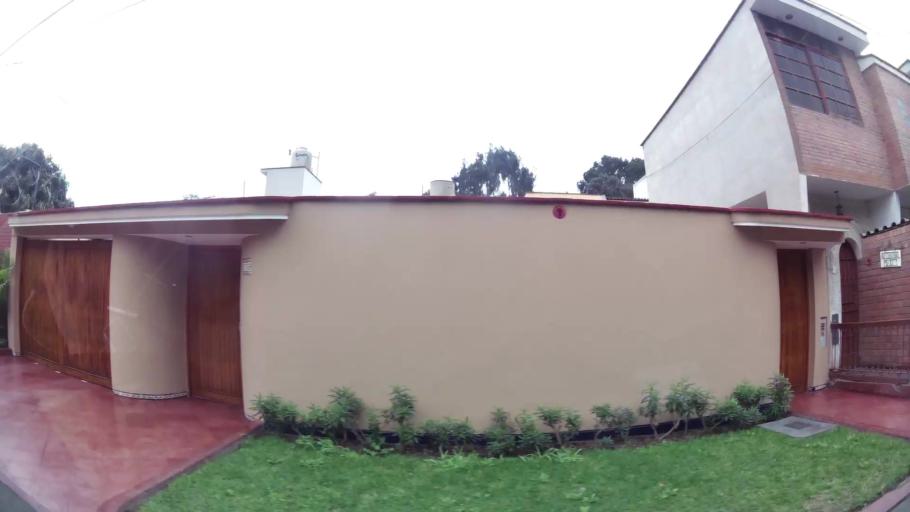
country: PE
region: Lima
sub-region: Lima
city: La Molina
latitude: -12.1086
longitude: -76.9619
